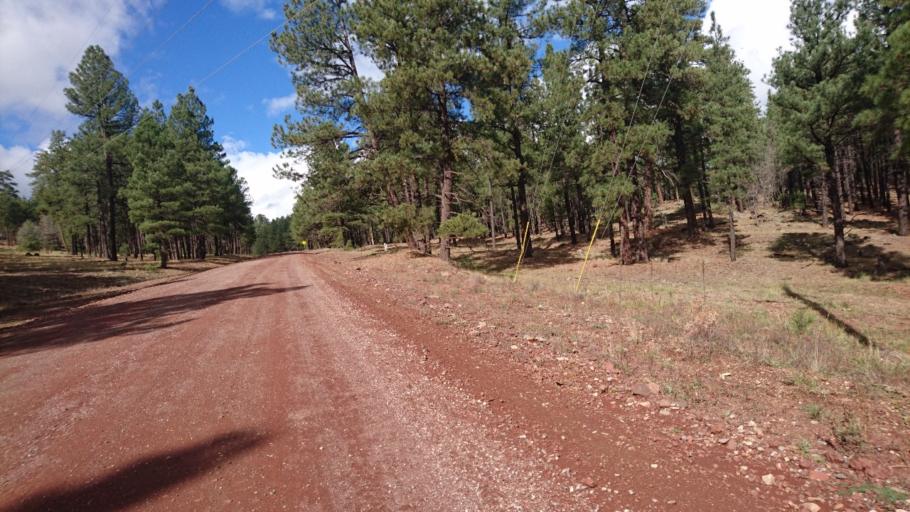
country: US
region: Arizona
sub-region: Coconino County
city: Parks
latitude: 35.2740
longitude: -111.8963
